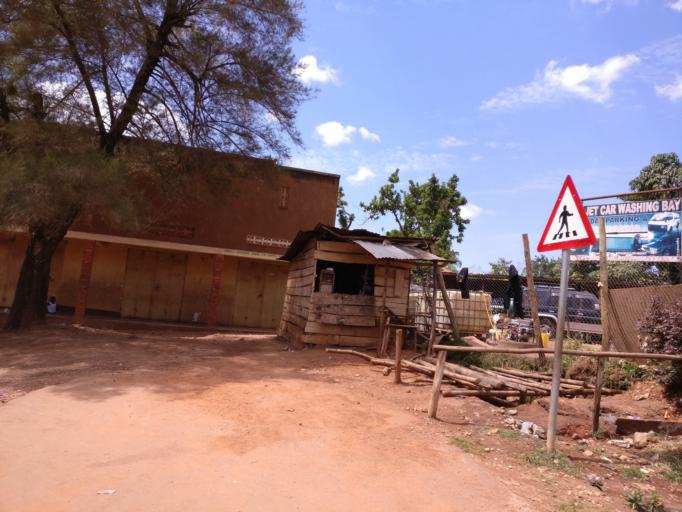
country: UG
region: Central Region
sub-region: Kampala District
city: Kampala
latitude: 0.2808
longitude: 32.5621
